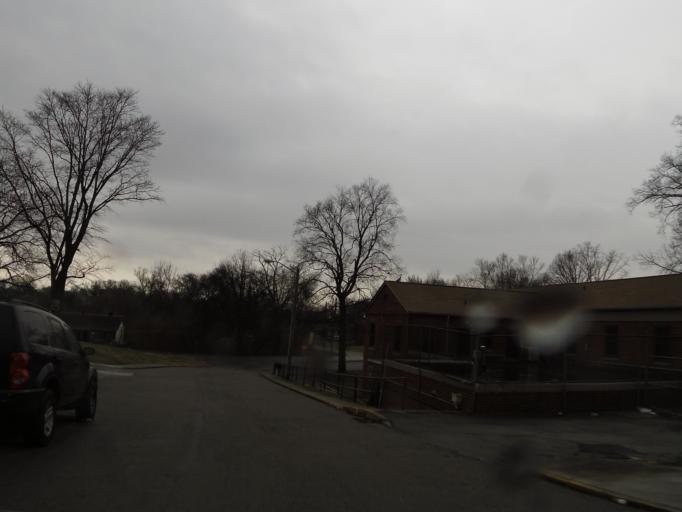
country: US
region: Tennessee
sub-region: Knox County
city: Knoxville
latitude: 35.9757
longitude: -83.9486
